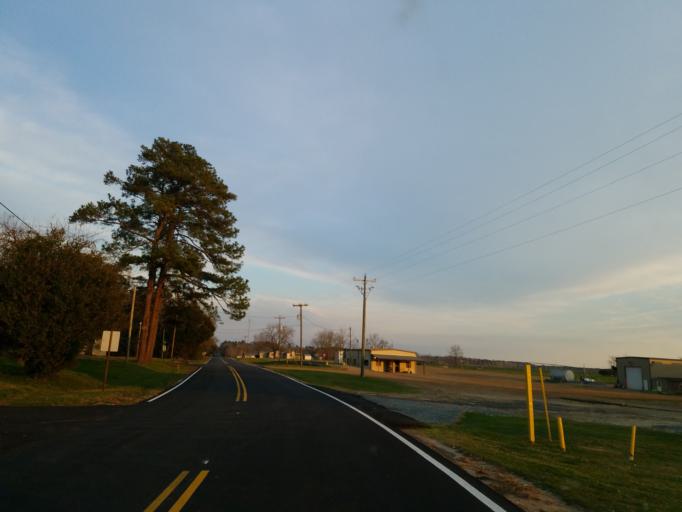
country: US
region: Georgia
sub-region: Colquitt County
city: Moultrie
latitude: 31.0648
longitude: -83.6234
